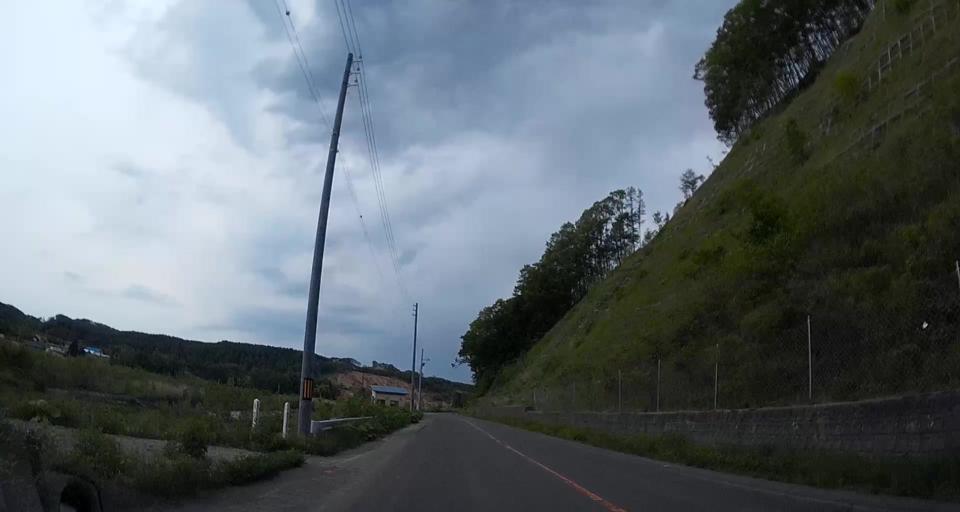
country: JP
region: Hokkaido
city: Chitose
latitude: 42.7596
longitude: 141.9491
